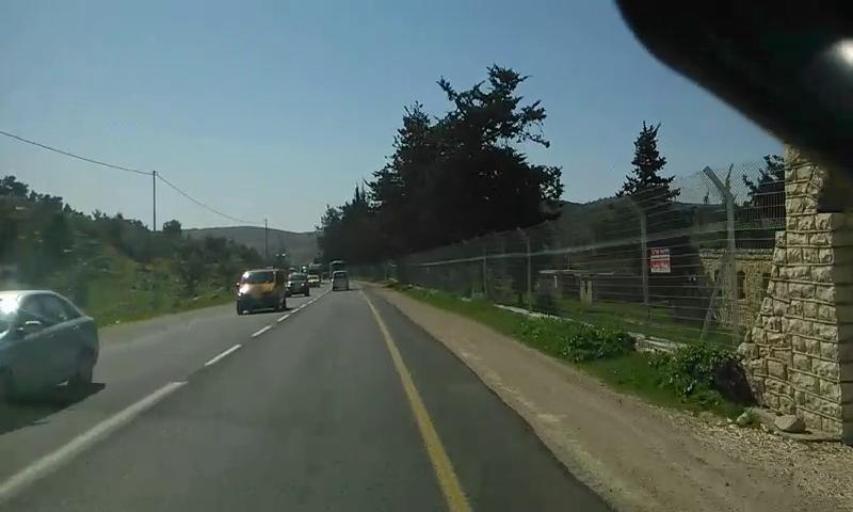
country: PS
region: West Bank
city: Shuyukh al `Arrub
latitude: 31.6316
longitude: 35.1320
